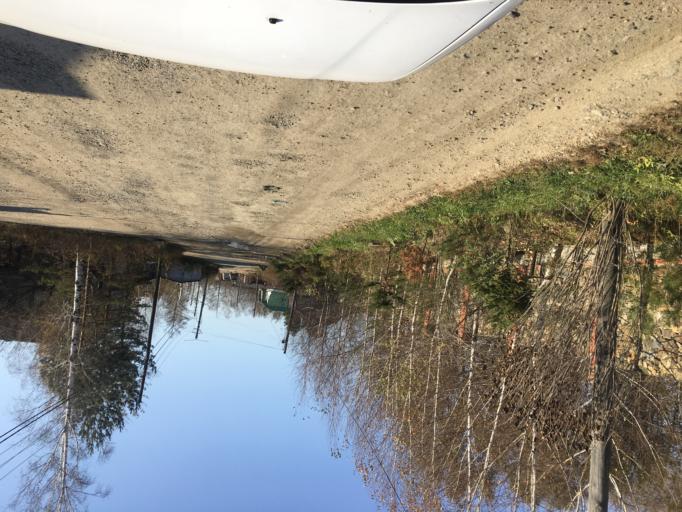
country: RU
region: Primorskiy
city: Dal'nerechensk
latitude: 45.9220
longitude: 133.7272
